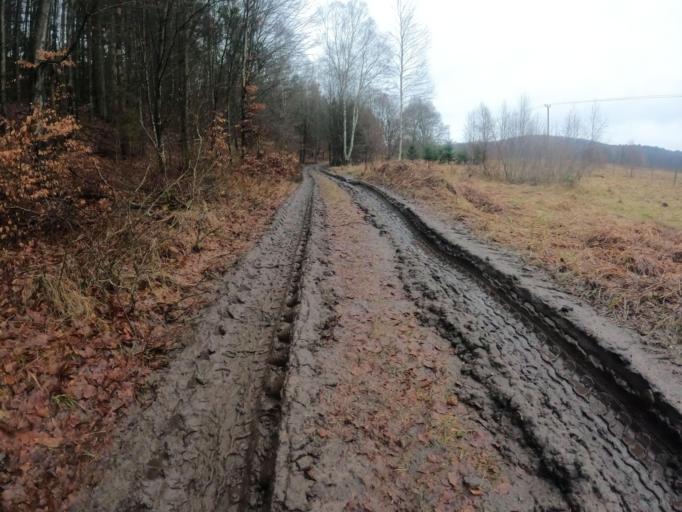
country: PL
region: West Pomeranian Voivodeship
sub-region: Powiat koszalinski
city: Polanow
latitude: 54.2290
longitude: 16.7239
